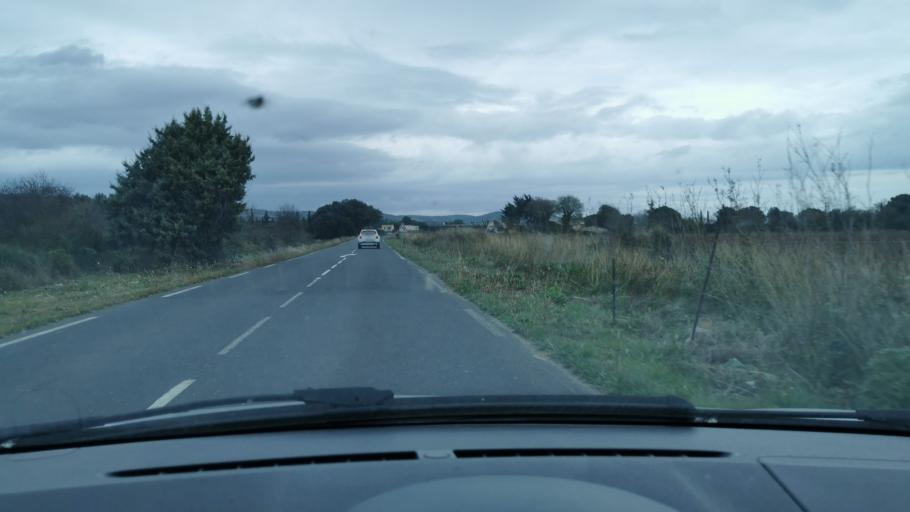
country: FR
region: Languedoc-Roussillon
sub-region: Departement de l'Herault
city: Balaruc-le-Vieux
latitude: 43.4402
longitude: 3.7124
